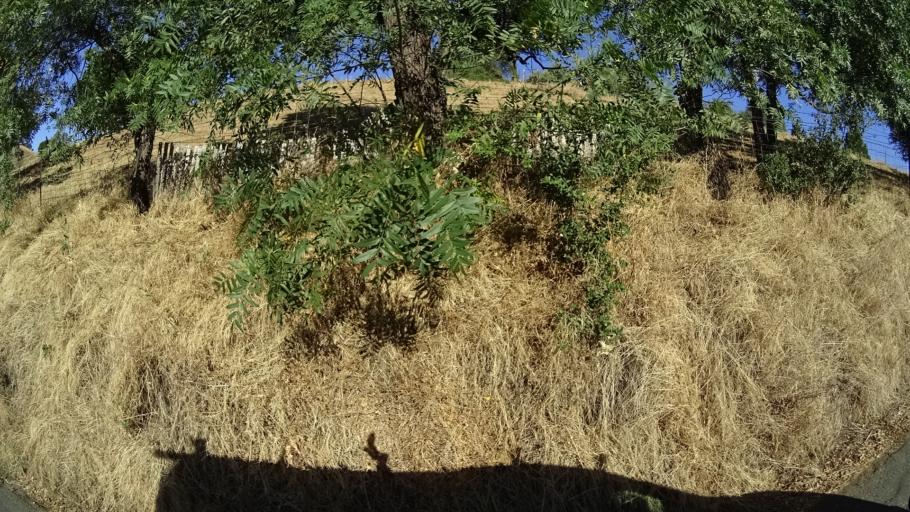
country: US
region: California
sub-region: Calaveras County
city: Angels Camp
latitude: 38.0386
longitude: -120.5052
